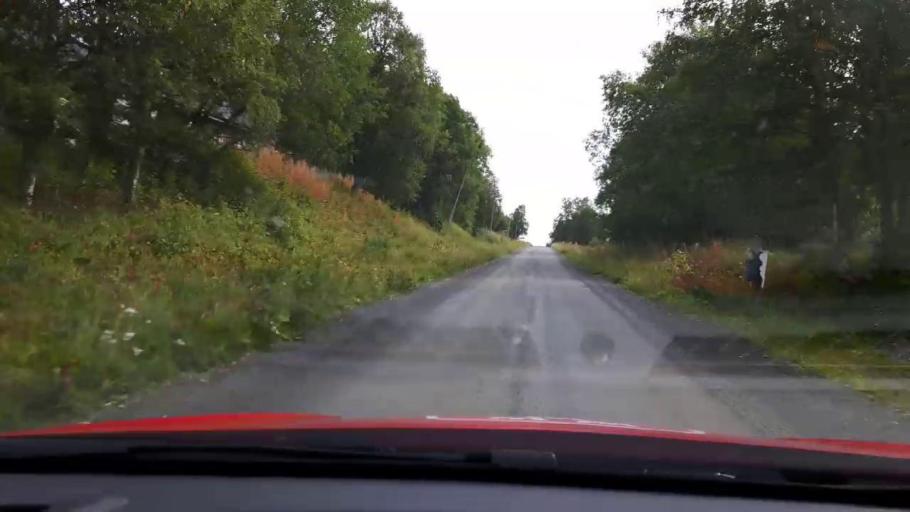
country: SE
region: Jaemtland
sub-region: Are Kommun
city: Are
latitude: 63.7494
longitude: 12.9620
